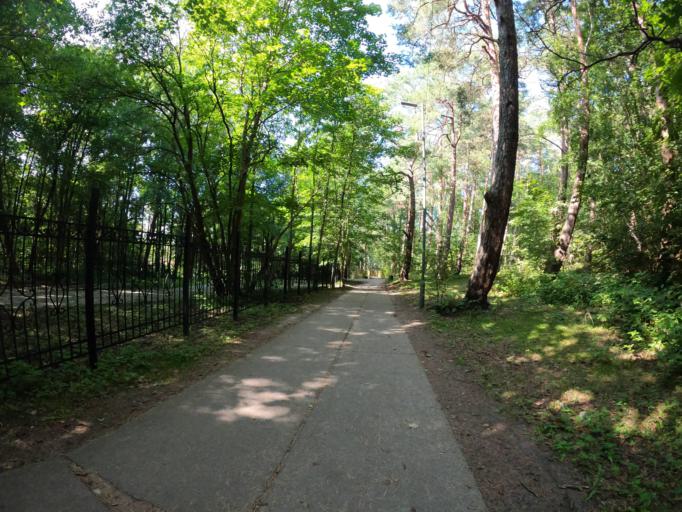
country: RU
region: Kaliningrad
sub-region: Gorod Svetlogorsk
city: Svetlogorsk
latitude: 54.9362
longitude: 20.1589
